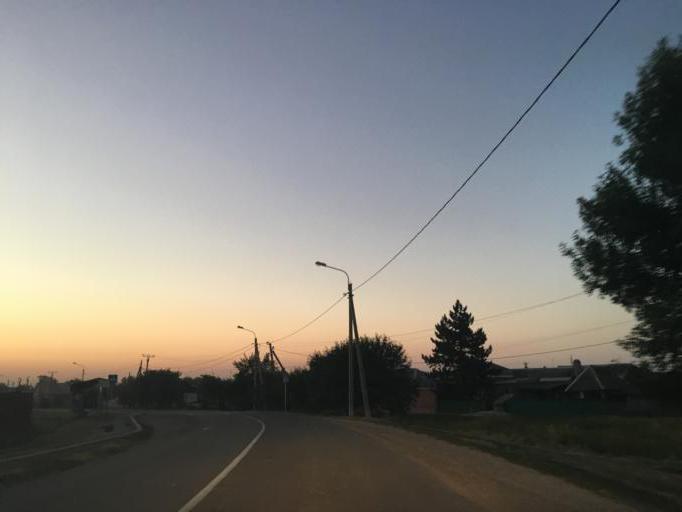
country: RU
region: Krasnodarskiy
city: Kushchevskaya
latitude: 46.5458
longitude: 39.6336
